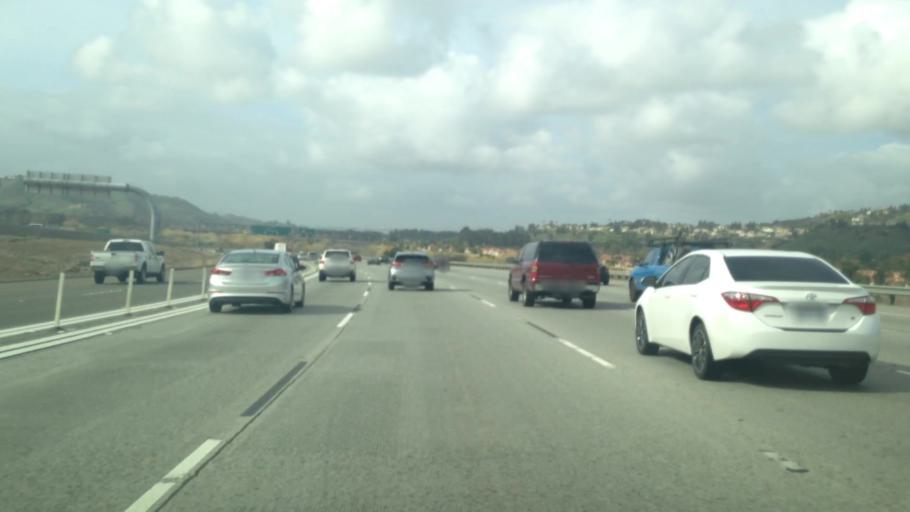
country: US
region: California
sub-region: San Bernardino County
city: Los Serranos
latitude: 33.8743
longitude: -117.6933
